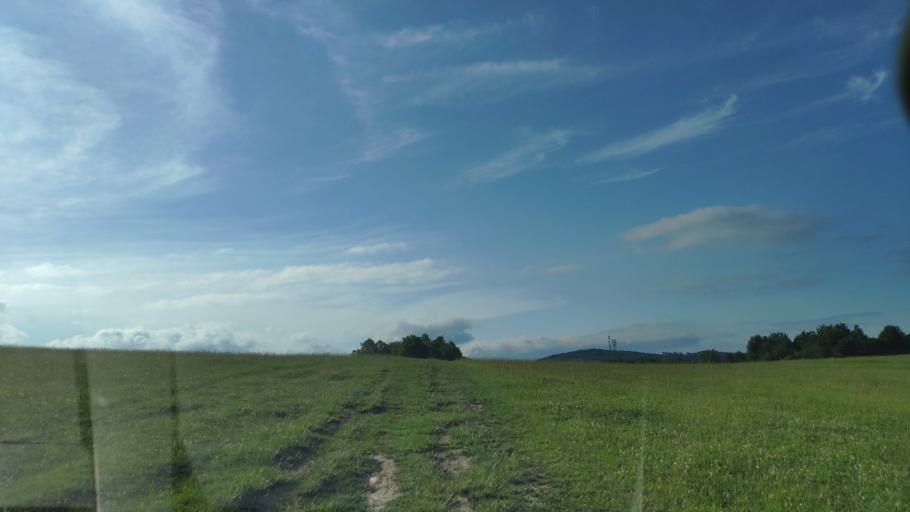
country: SK
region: Presovsky
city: Vranov nad Topl'ou
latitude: 48.8224
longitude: 21.5878
